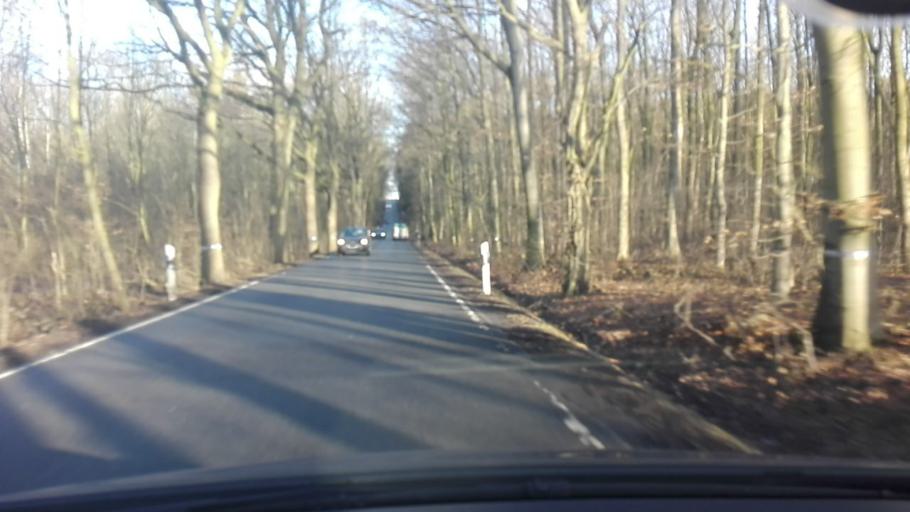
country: DE
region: North Rhine-Westphalia
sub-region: Regierungsbezirk Arnsberg
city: Frondenberg
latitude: 51.4933
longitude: 7.7531
